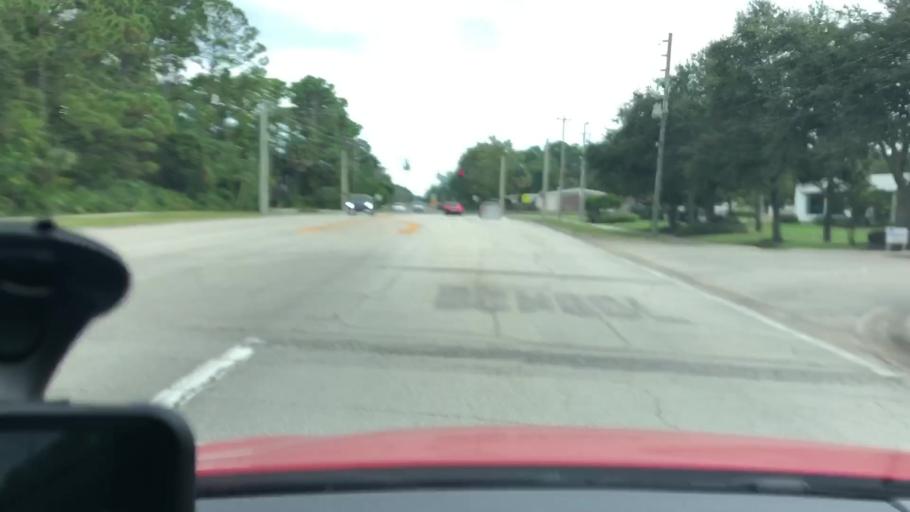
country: US
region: Florida
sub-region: Volusia County
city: Daytona Beach
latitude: 29.2006
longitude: -81.0721
